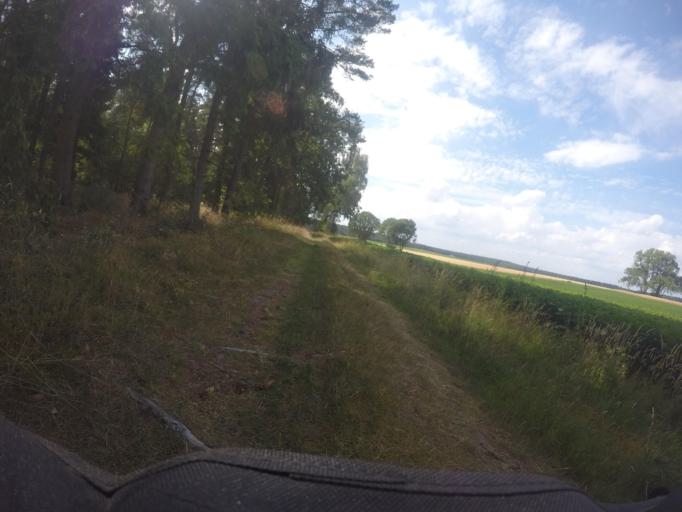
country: DE
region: Lower Saxony
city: Dahlem
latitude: 53.2230
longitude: 10.7455
